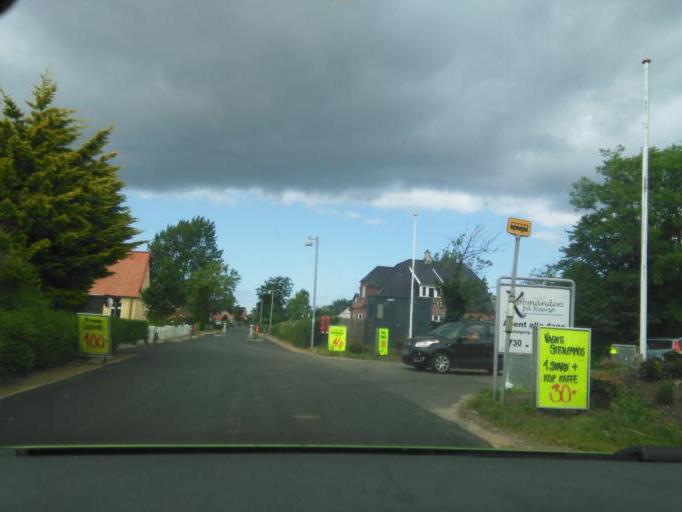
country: DK
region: Zealand
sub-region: Kalundborg Kommune
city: Gorlev
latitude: 55.5210
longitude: 11.1142
